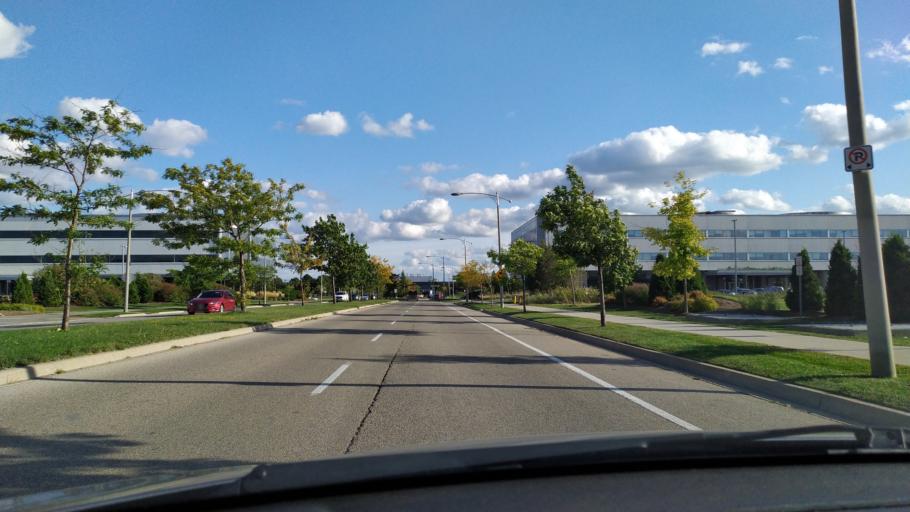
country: CA
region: Ontario
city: Waterloo
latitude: 43.4788
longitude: -80.5493
